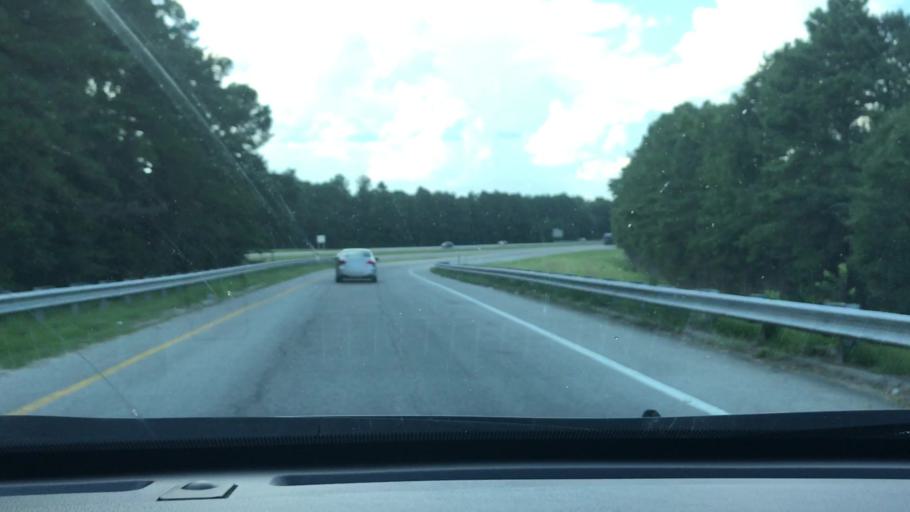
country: US
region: South Carolina
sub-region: Sumter County
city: East Sumter
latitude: 33.9012
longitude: -80.0918
